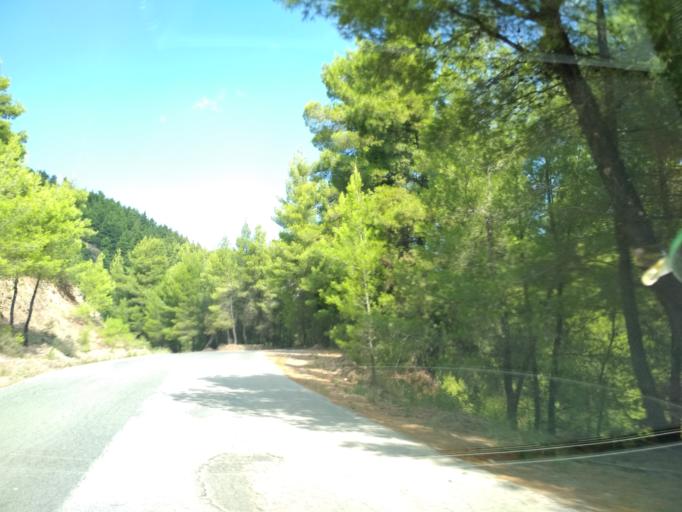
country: GR
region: Central Greece
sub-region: Nomos Evvoias
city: Roviai
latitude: 38.8384
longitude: 23.2859
